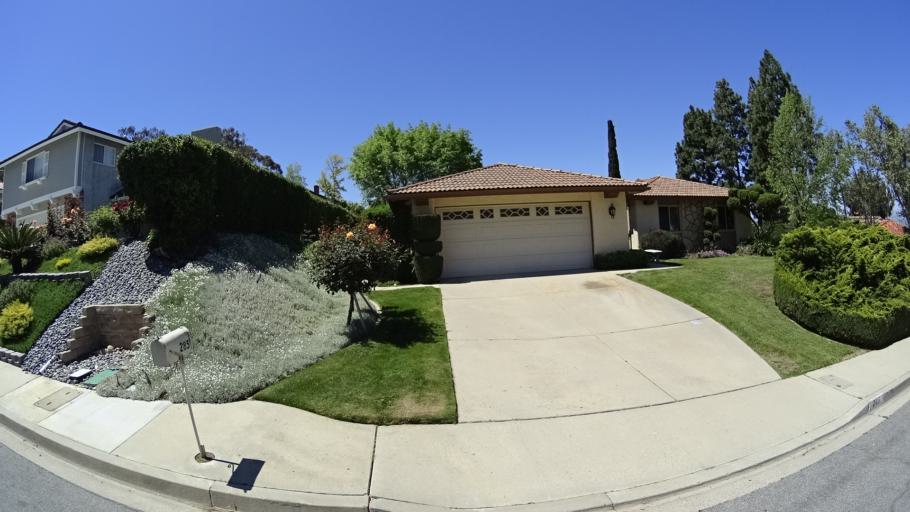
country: US
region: California
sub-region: Ventura County
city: Casa Conejo
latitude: 34.1748
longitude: -118.8961
